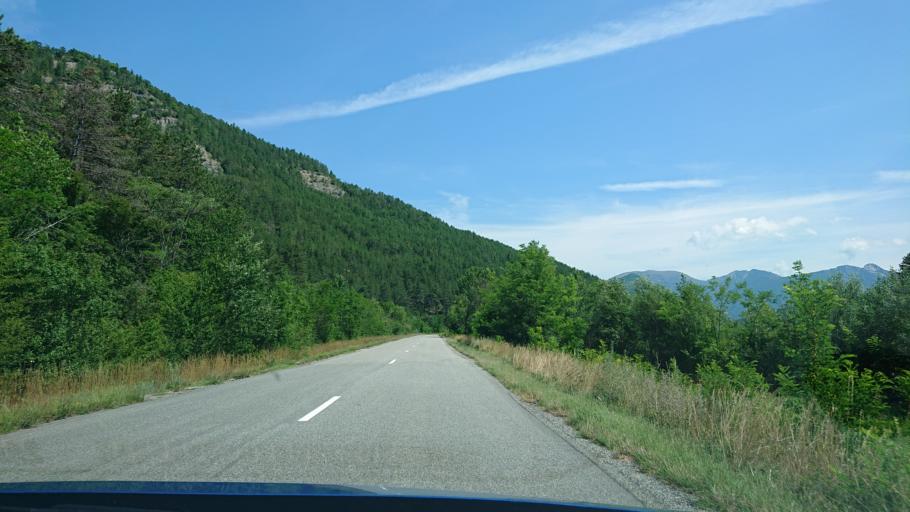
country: FR
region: Provence-Alpes-Cote d'Azur
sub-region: Departement des Alpes-de-Haute-Provence
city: Sisteron
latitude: 44.2931
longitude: 6.0273
